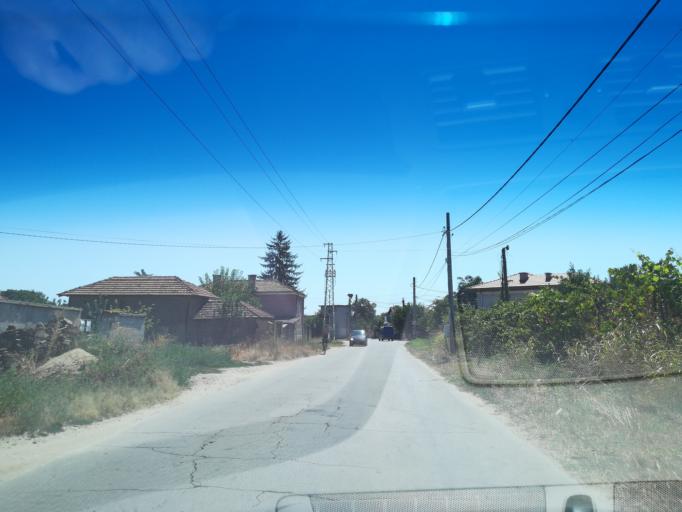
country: BG
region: Pazardzhik
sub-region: Obshtina Pazardzhik
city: Pazardzhik
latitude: 42.2804
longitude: 24.3949
